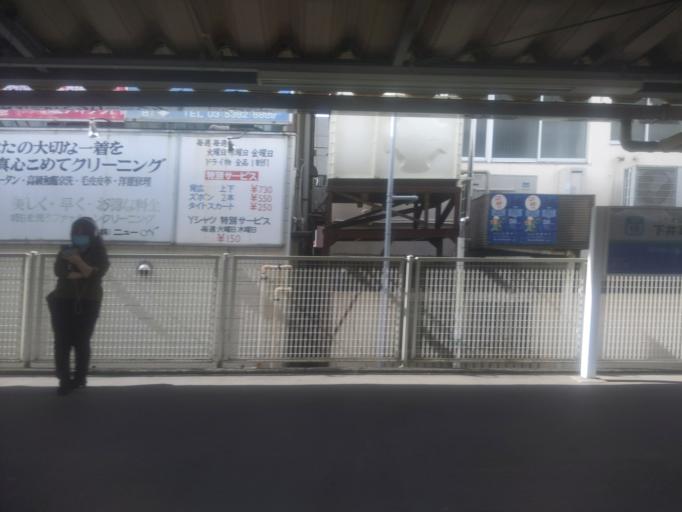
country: JP
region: Saitama
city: Wako
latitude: 35.7238
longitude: 139.6253
